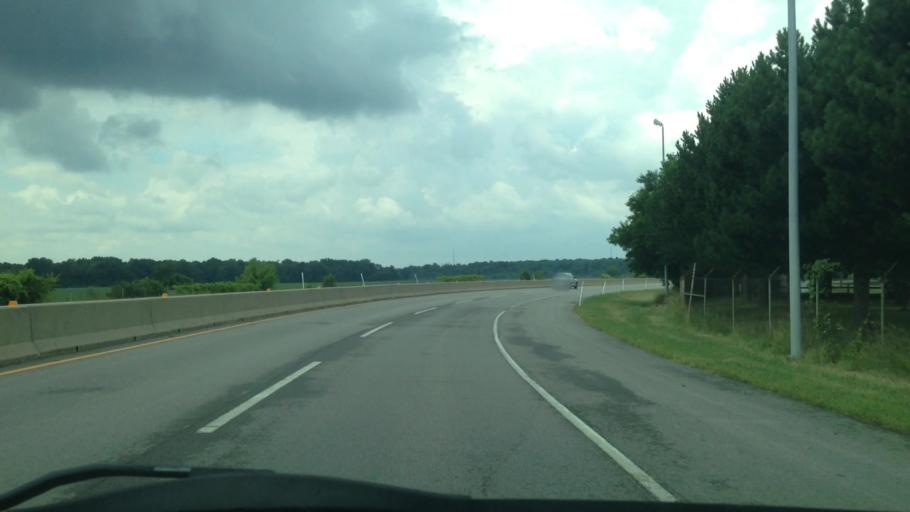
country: US
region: Indiana
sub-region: Saint Joseph County
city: Notre Dame
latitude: 41.7132
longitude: -86.2550
